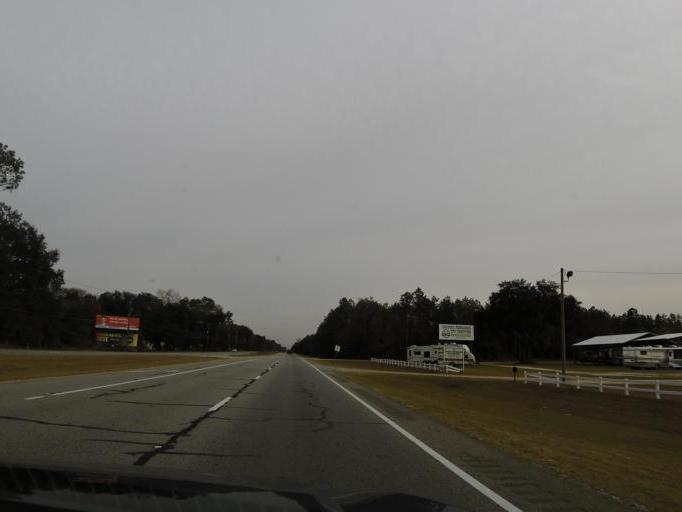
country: US
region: Georgia
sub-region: Decatur County
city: Bainbridge
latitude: 30.9330
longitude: -84.6451
